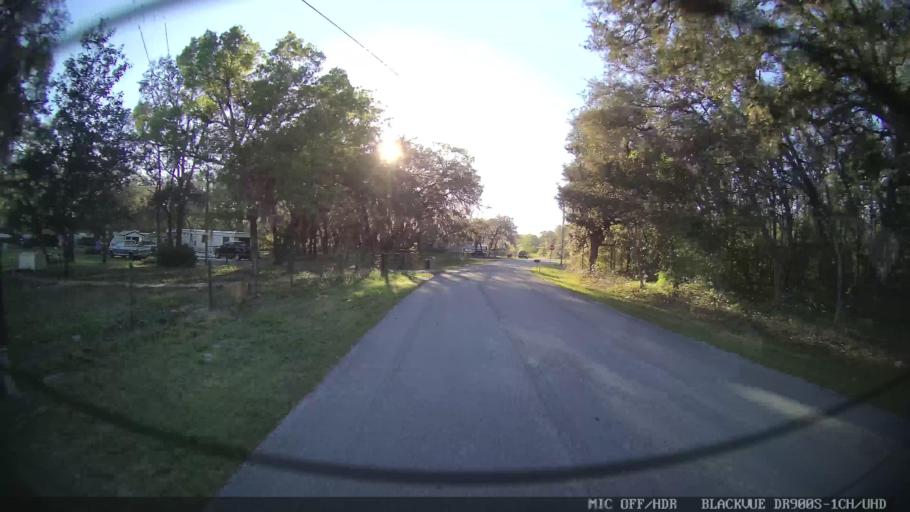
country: US
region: Florida
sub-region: Pasco County
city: Shady Hills
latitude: 28.4176
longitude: -82.5770
